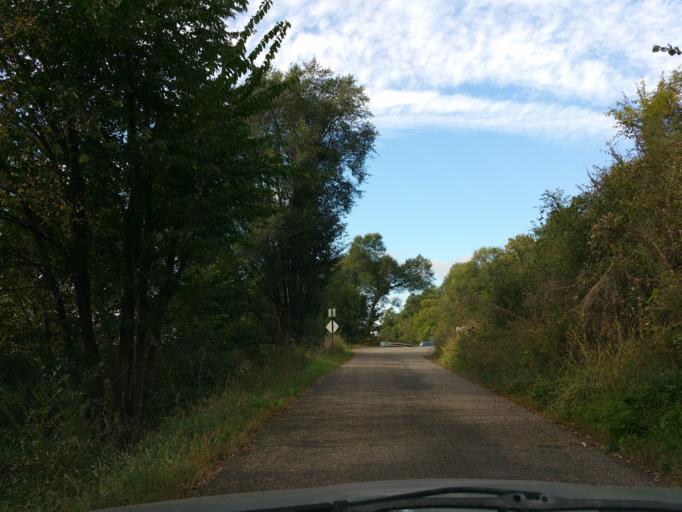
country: US
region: Wisconsin
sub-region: Pierce County
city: Prescott
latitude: 44.7444
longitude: -92.7956
